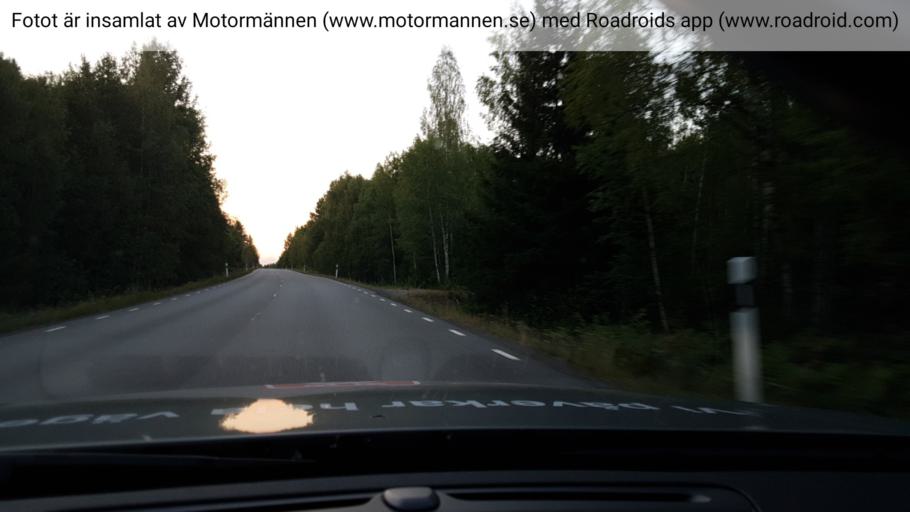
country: SE
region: Uppsala
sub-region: Heby Kommun
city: OEstervala
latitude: 60.1320
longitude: 17.2196
